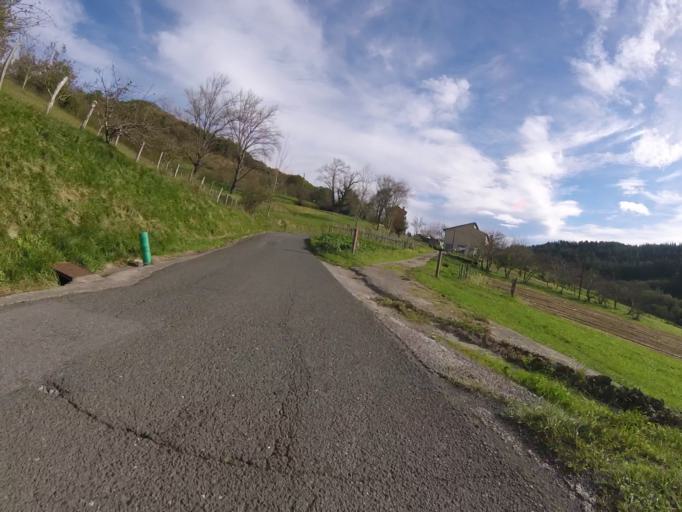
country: ES
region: Basque Country
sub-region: Provincia de Guipuzcoa
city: Orio
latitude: 43.2846
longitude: -2.1089
